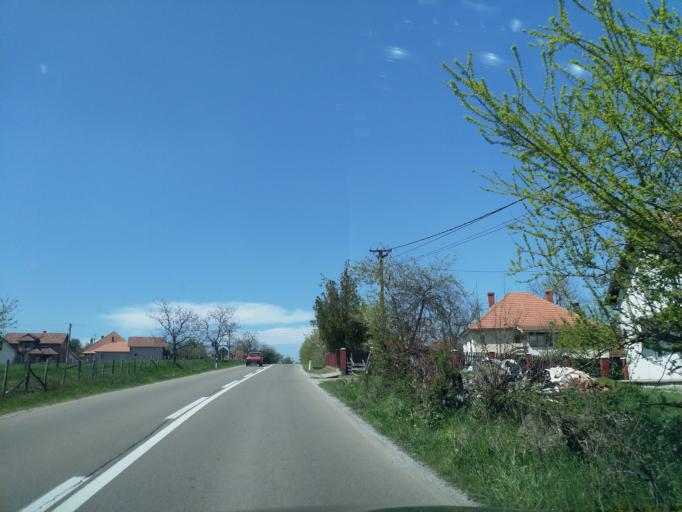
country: RS
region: Central Serbia
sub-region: Belgrade
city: Lazarevac
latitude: 44.3489
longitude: 20.3858
